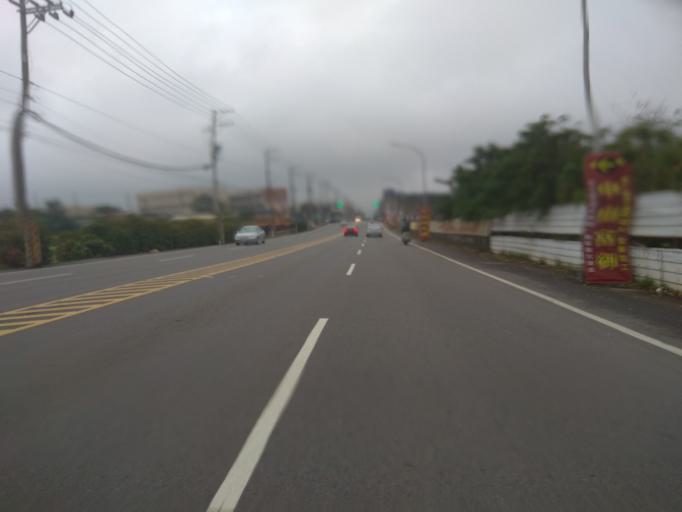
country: TW
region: Taiwan
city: Taoyuan City
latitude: 25.0282
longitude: 121.1084
